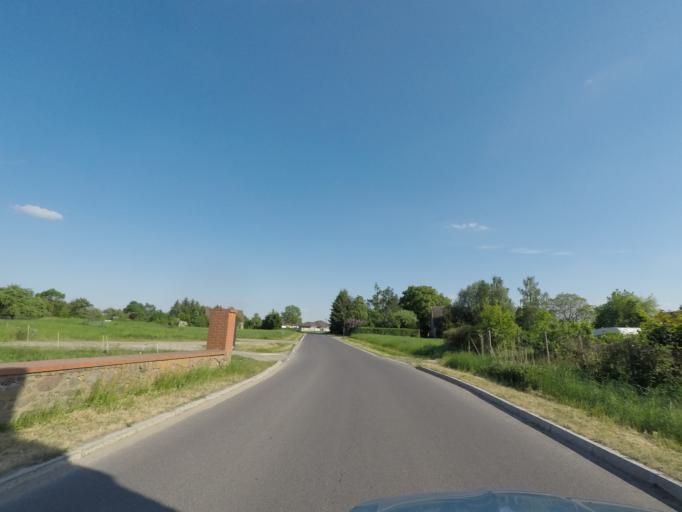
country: DE
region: Brandenburg
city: Hohenfinow
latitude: 52.7280
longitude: 13.8716
